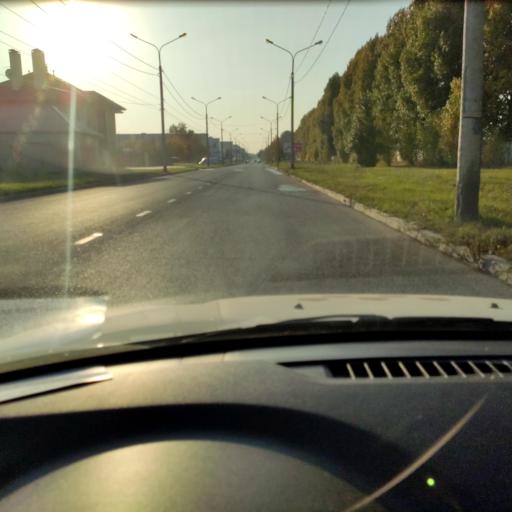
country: RU
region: Samara
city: Tol'yatti
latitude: 53.5411
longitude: 49.4180
